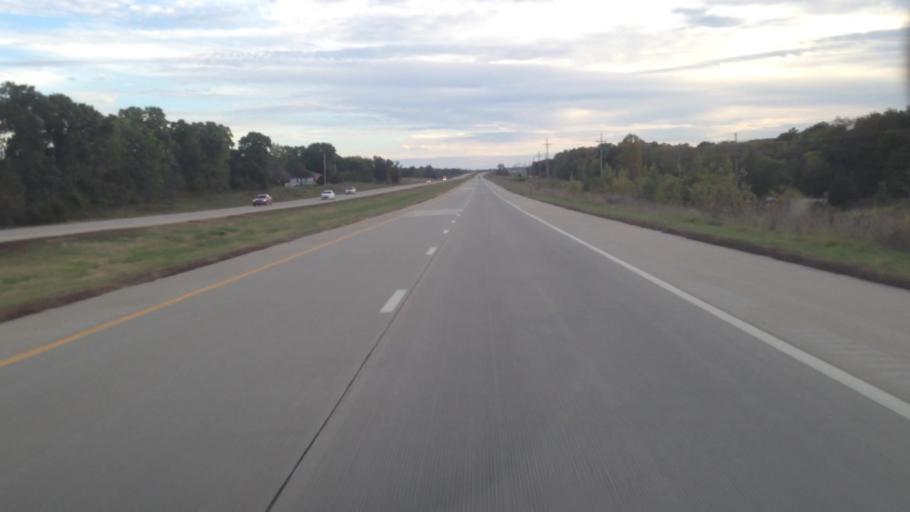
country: US
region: Kansas
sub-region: Douglas County
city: Baldwin City
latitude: 38.7563
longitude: -95.2682
